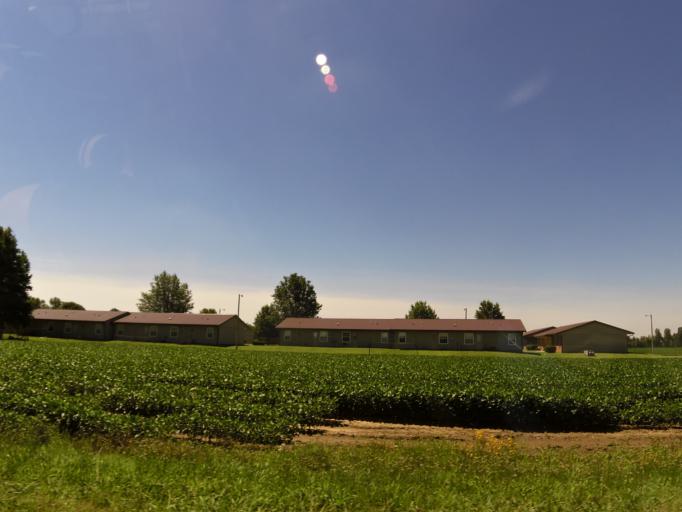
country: US
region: Missouri
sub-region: New Madrid County
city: Lilbourn
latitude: 36.5671
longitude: -89.6032
